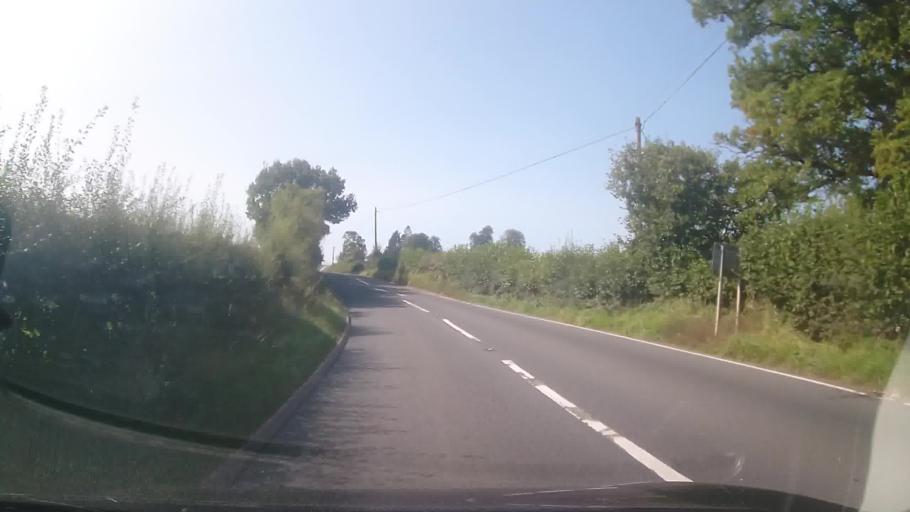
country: GB
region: Wales
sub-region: Sir Powys
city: Builth Wells
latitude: 52.1518
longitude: -3.4632
